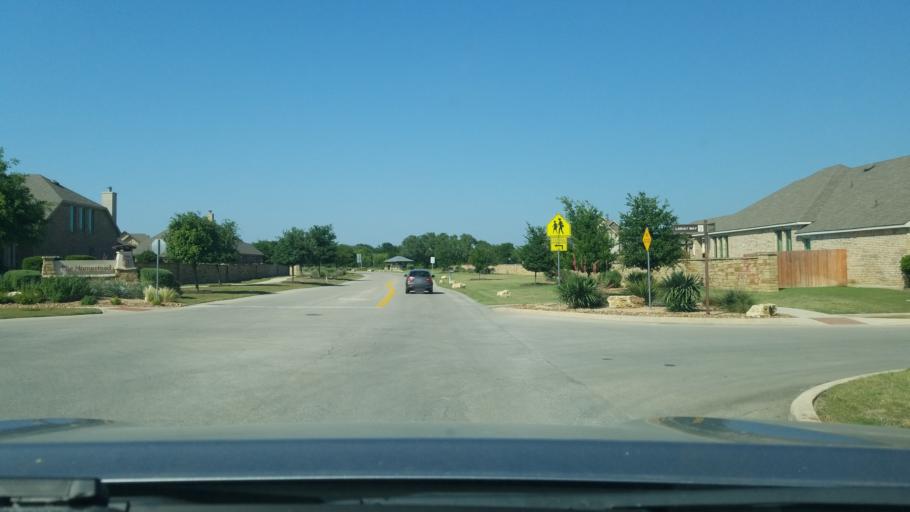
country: US
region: Texas
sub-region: Comal County
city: Bulverde
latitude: 29.7503
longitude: -98.4188
